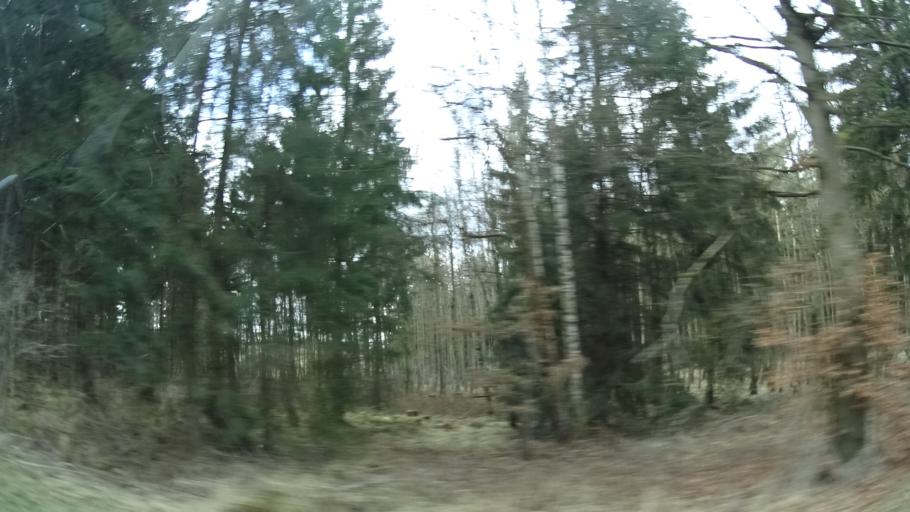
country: DE
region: Thuringia
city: Bobeck
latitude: 50.9021
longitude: 11.8120
